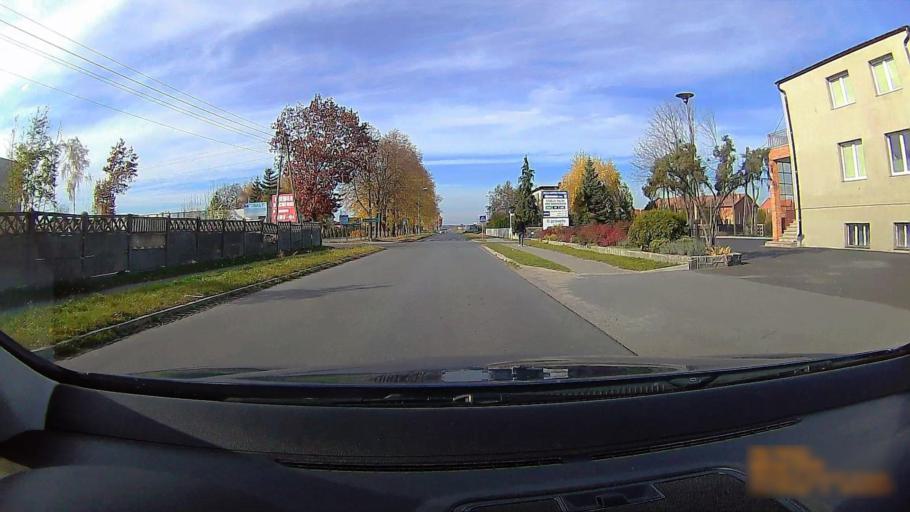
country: PL
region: Greater Poland Voivodeship
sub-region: Powiat ostrzeszowski
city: Doruchow
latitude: 51.4177
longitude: 18.0736
